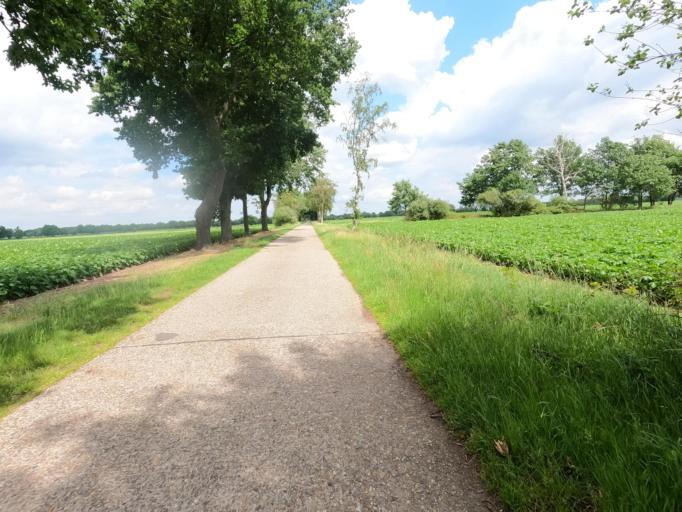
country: BE
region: Flanders
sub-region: Provincie Antwerpen
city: Kalmthout
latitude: 51.4138
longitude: 4.5103
